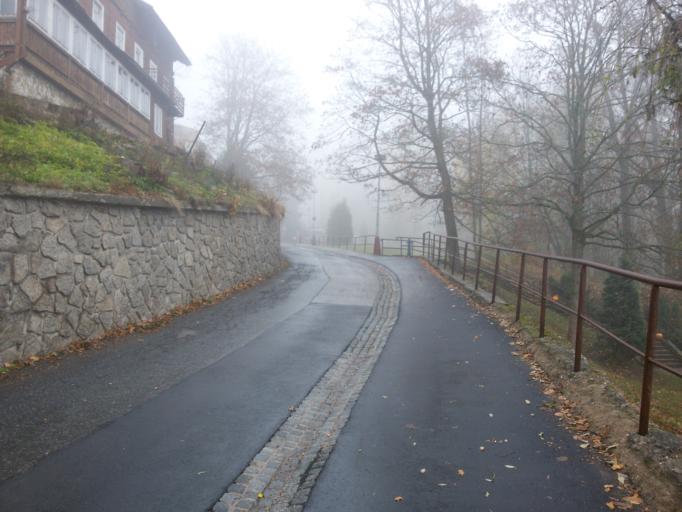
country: CZ
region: Kralovehradecky
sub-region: Okres Trutnov
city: Svoboda nad Upou
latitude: 50.6315
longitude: 15.7826
